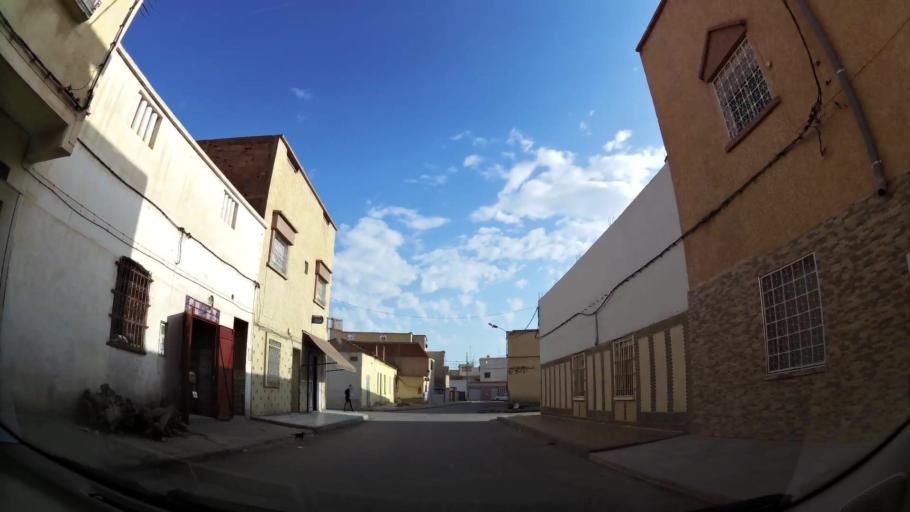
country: MA
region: Oriental
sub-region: Oujda-Angad
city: Oujda
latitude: 34.6710
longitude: -1.9255
